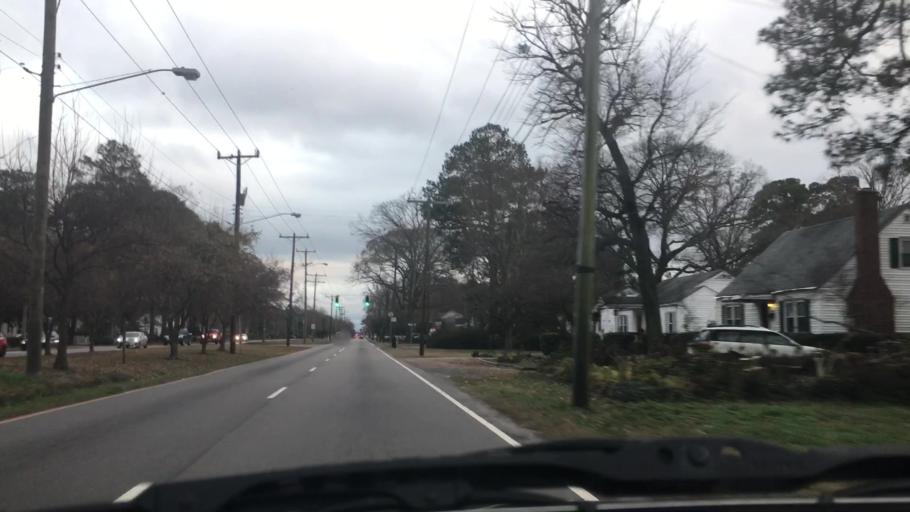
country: US
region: Virginia
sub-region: City of Norfolk
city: Norfolk
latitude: 36.9246
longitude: -76.2432
